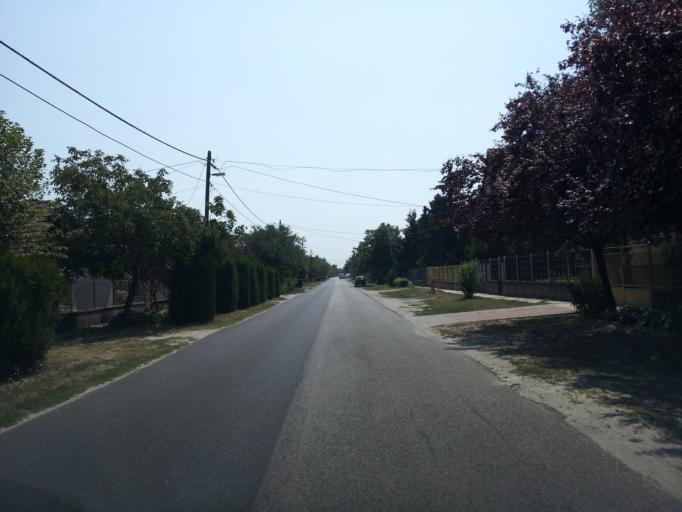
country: HU
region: Pest
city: Dunavarsany
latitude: 47.2812
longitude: 19.0686
